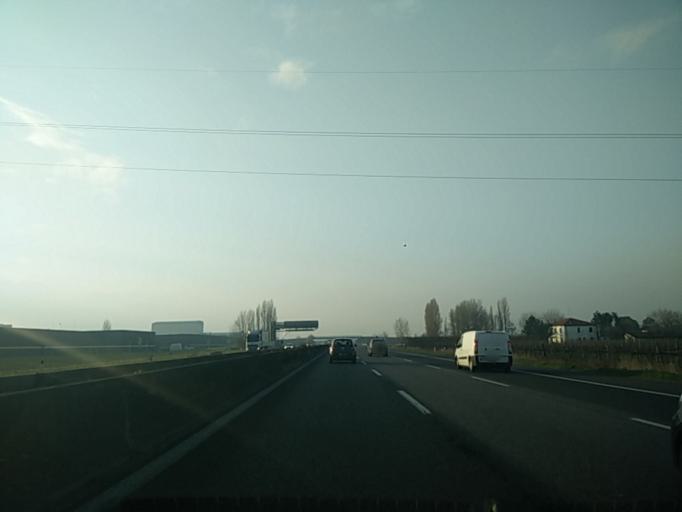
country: IT
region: Emilia-Romagna
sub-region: Provincia di Ravenna
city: Faenza
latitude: 44.3296
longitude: 11.8903
